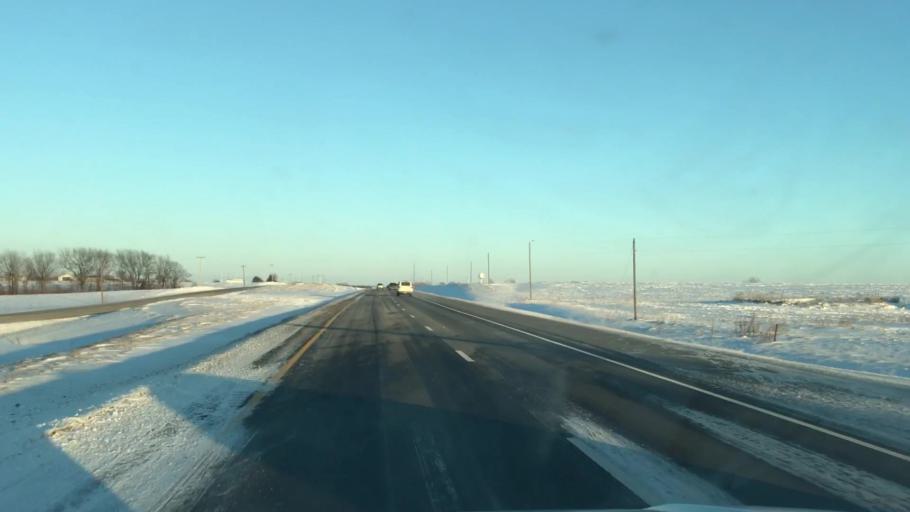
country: US
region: Missouri
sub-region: Clinton County
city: Gower
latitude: 39.7620
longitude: -94.5262
